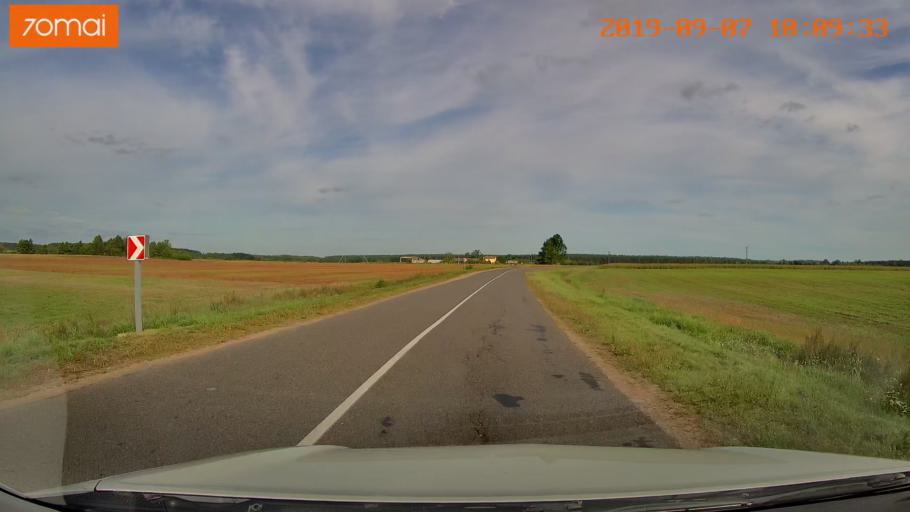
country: BY
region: Grodnenskaya
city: Voranava
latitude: 54.0966
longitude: 25.3731
